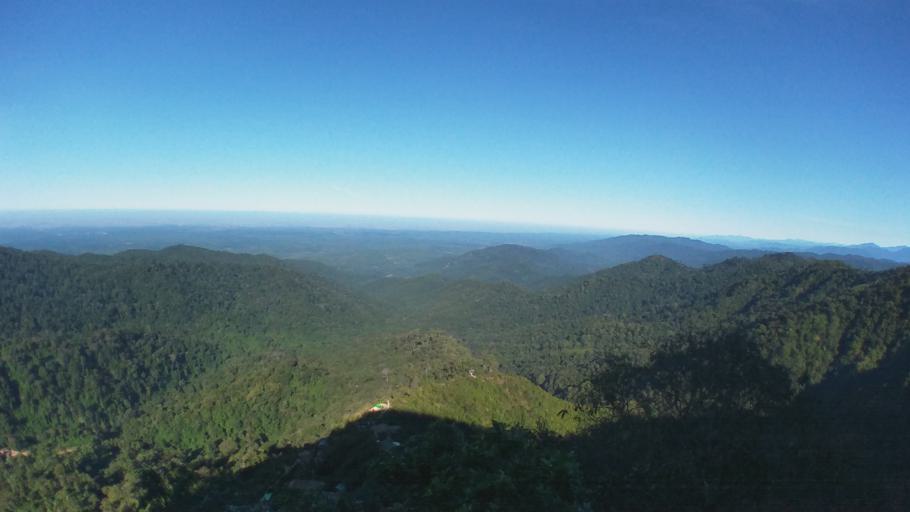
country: MM
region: Mon
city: Kyaikto
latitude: 17.4838
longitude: 97.0958
